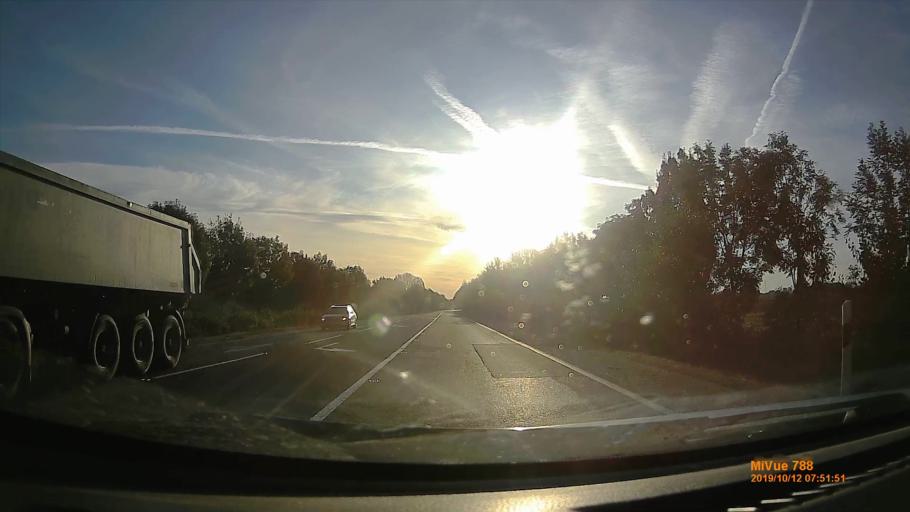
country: HU
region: Hajdu-Bihar
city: Biharkeresztes
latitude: 47.1394
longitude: 21.7316
